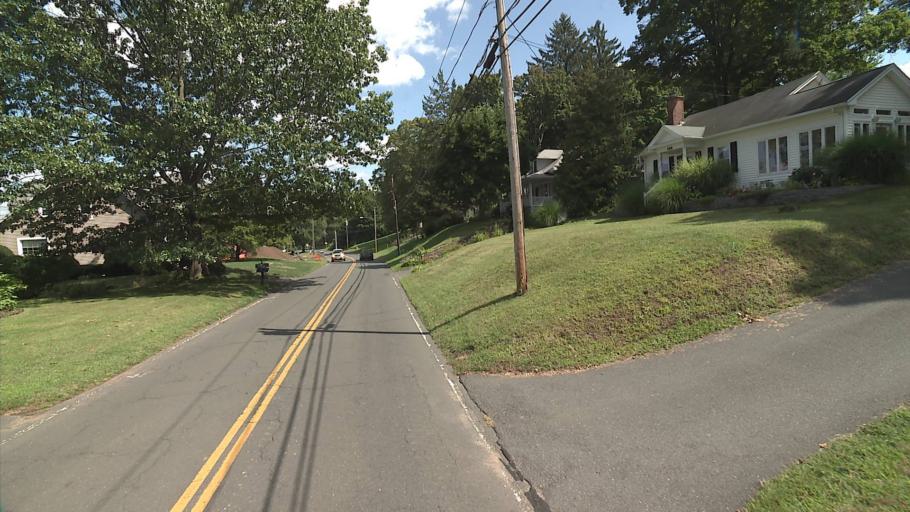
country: US
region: Connecticut
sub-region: Hartford County
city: Glastonbury Center
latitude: 41.6657
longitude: -72.6127
